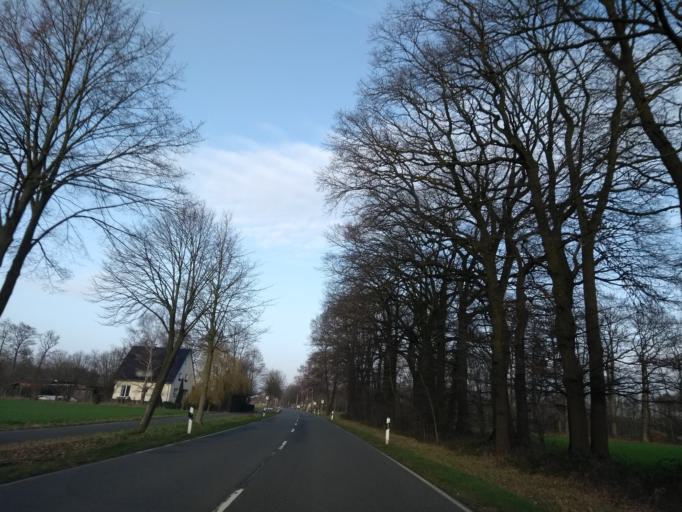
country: DE
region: North Rhine-Westphalia
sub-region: Regierungsbezirk Detmold
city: Hovelhof
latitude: 51.7979
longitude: 8.6658
